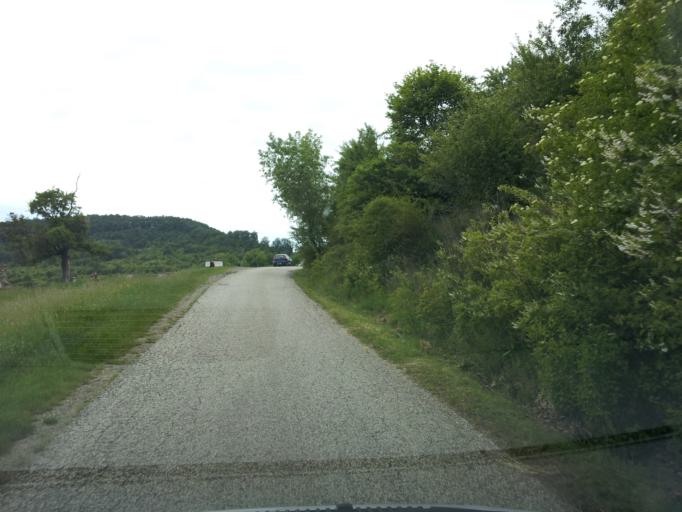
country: HU
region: Komarom-Esztergom
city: Kesztolc
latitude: 47.7339
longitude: 18.8441
